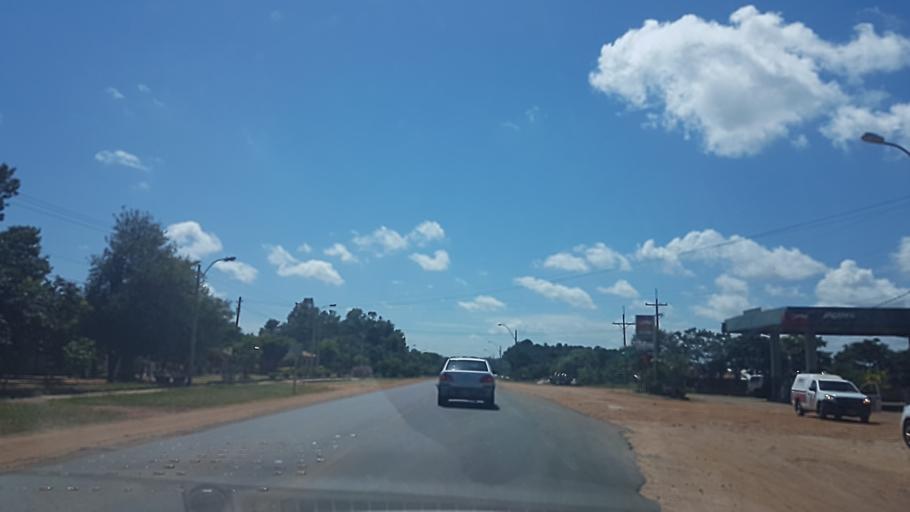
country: PY
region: Misiones
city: San Juan Bautista
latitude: -26.6732
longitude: -57.1183
